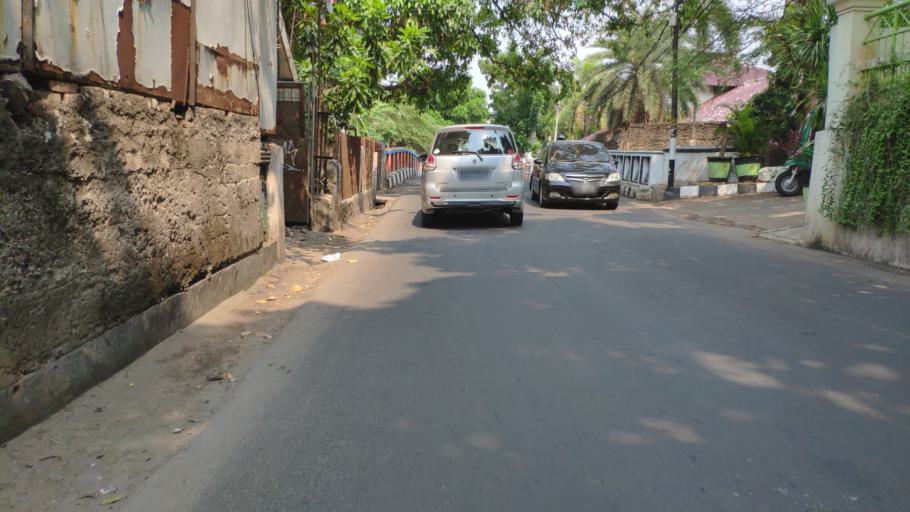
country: ID
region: Jakarta Raya
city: Jakarta
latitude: -6.2507
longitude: 106.8101
